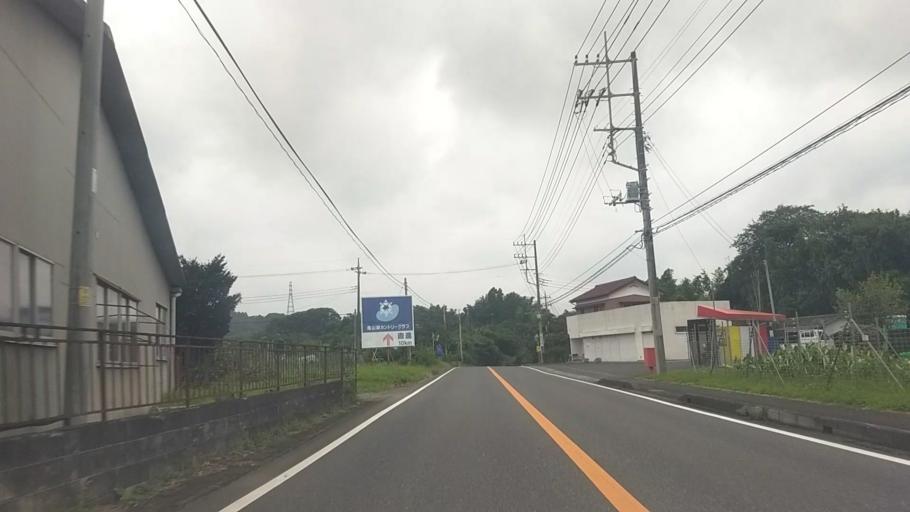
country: JP
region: Chiba
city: Kisarazu
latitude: 35.2769
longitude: 140.0720
